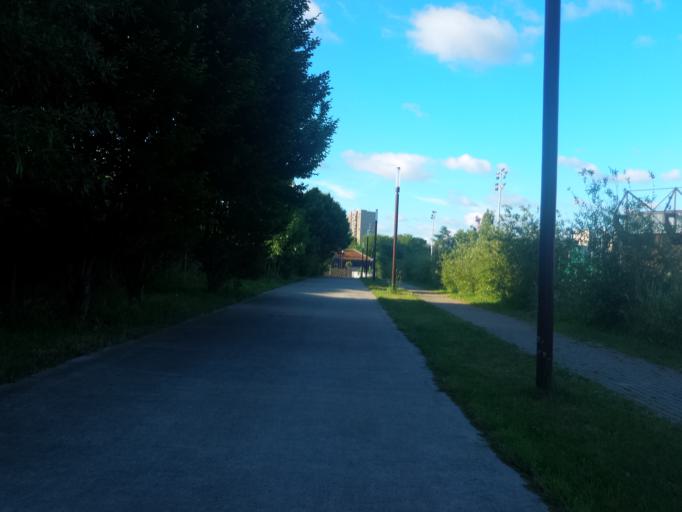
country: FR
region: Pays de la Loire
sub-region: Departement de la Loire-Atlantique
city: Nantes
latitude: 47.2090
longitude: -1.5344
